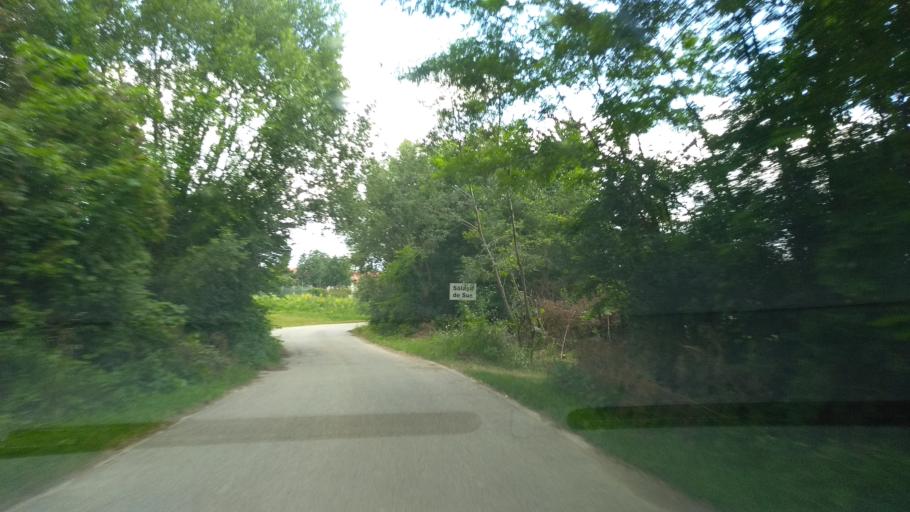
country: RO
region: Hunedoara
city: Salasu de Sus
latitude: 45.5066
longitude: 22.9580
